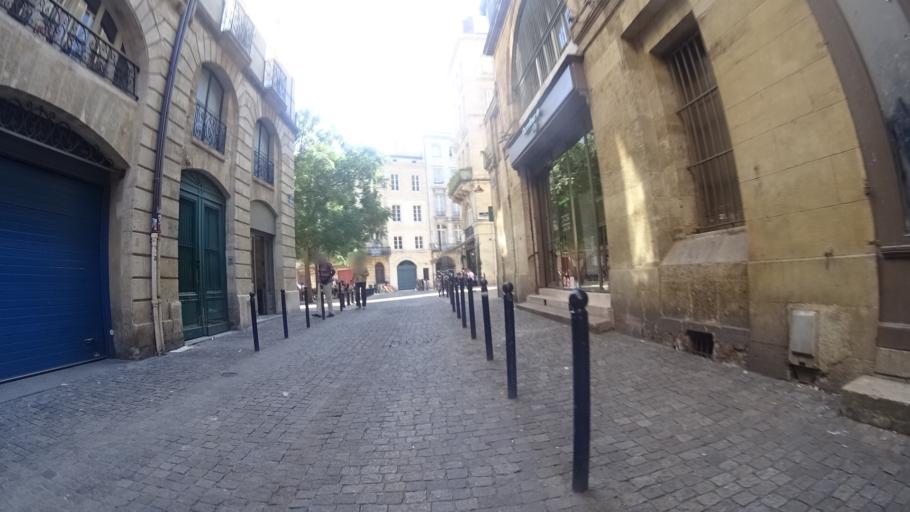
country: FR
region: Aquitaine
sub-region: Departement de la Gironde
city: Bordeaux
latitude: 44.8388
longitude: -0.5697
